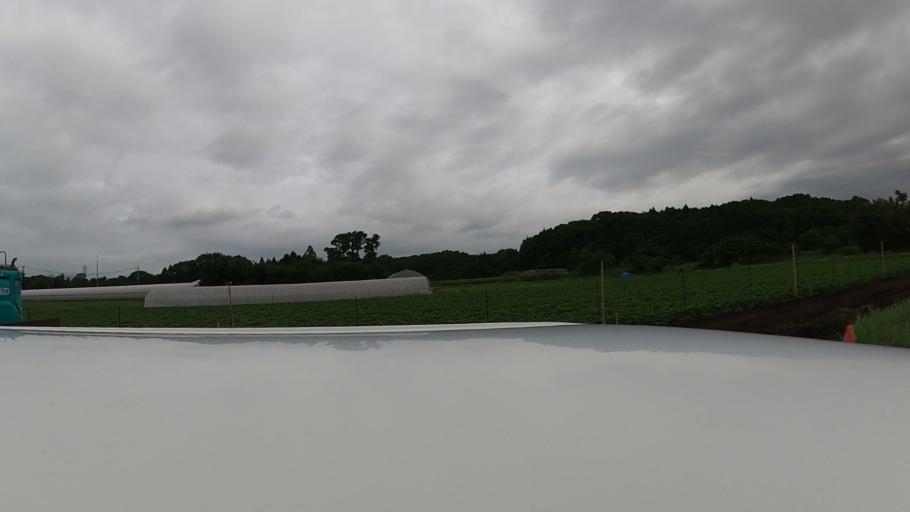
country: JP
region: Kumamoto
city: Ozu
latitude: 32.8305
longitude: 130.8611
